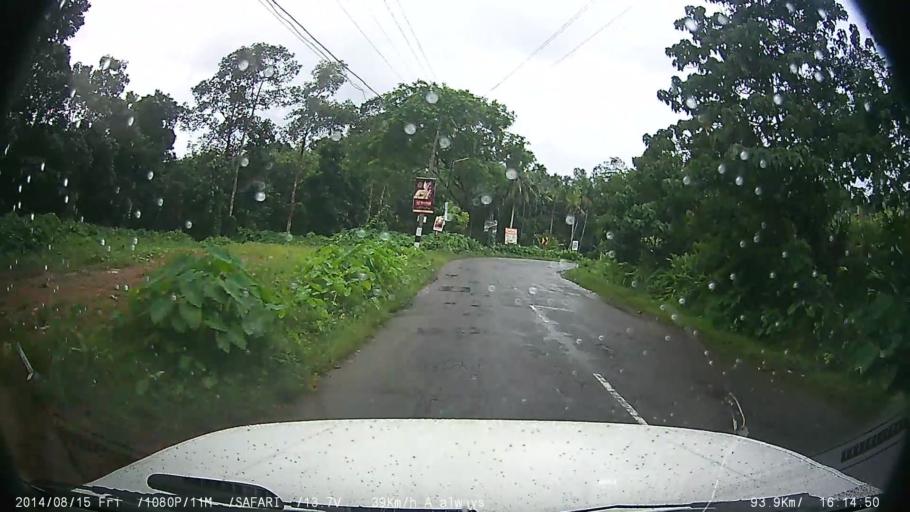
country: IN
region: Kerala
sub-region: Kottayam
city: Lalam
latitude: 9.7334
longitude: 76.6928
